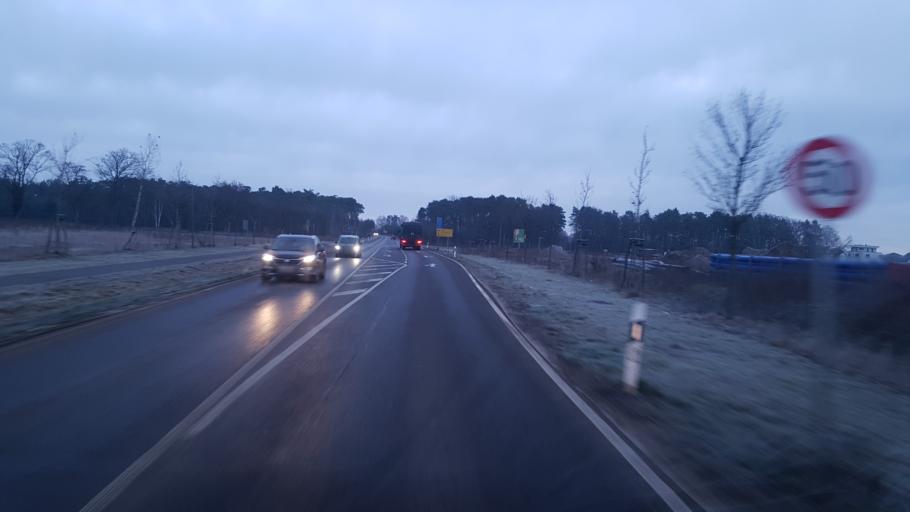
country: DE
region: Brandenburg
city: Ludwigsfelde
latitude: 52.3135
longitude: 13.2104
